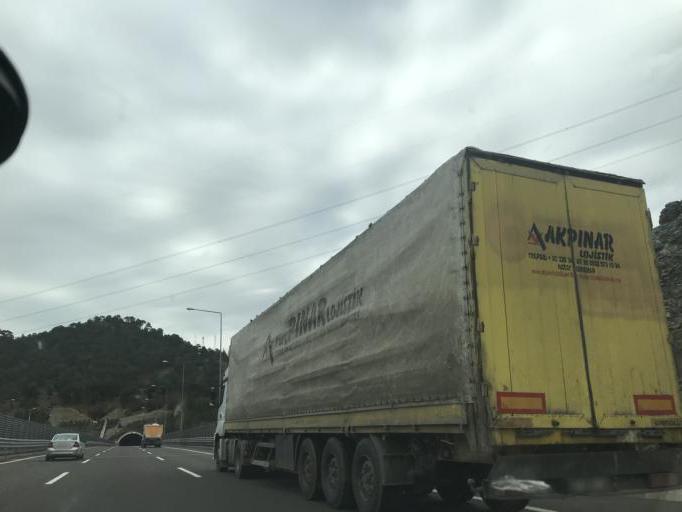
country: TR
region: Nigde
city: Ciftehan
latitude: 37.5054
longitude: 34.8213
